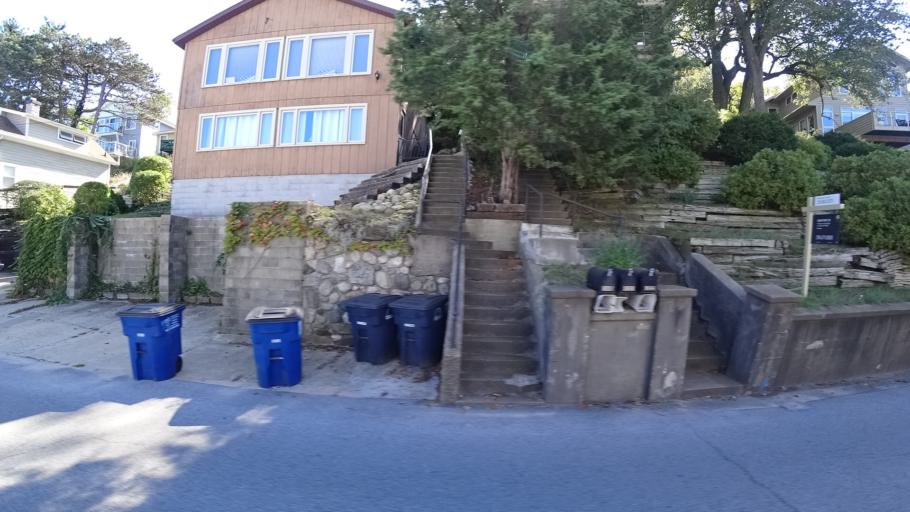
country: US
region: Indiana
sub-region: LaPorte County
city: Long Beach
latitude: 41.7360
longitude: -86.8767
